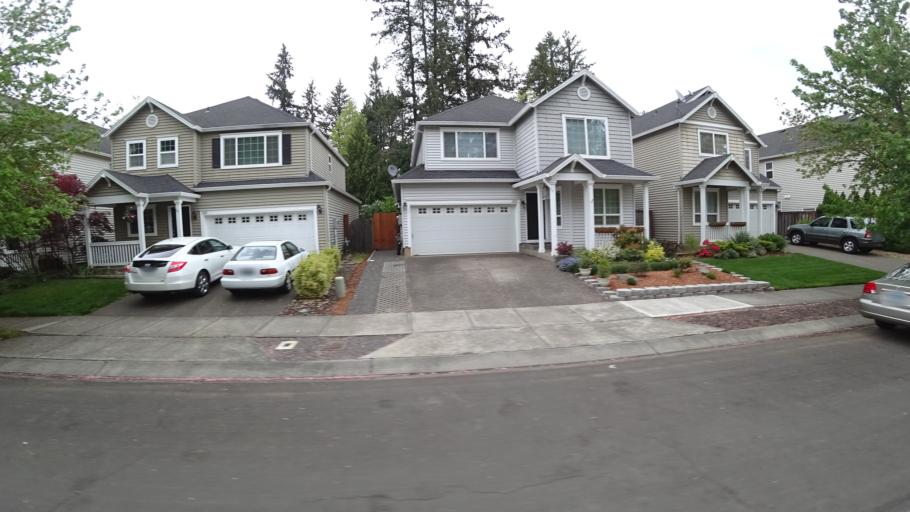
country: US
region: Oregon
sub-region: Washington County
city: Hillsboro
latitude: 45.5343
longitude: -122.9838
